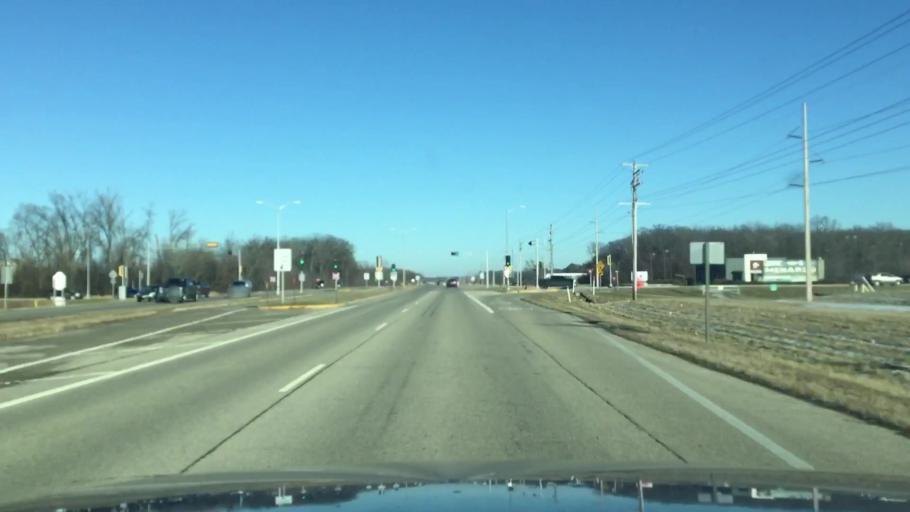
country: US
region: Wisconsin
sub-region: Racine County
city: Browns Lake
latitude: 42.7035
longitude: -88.2493
